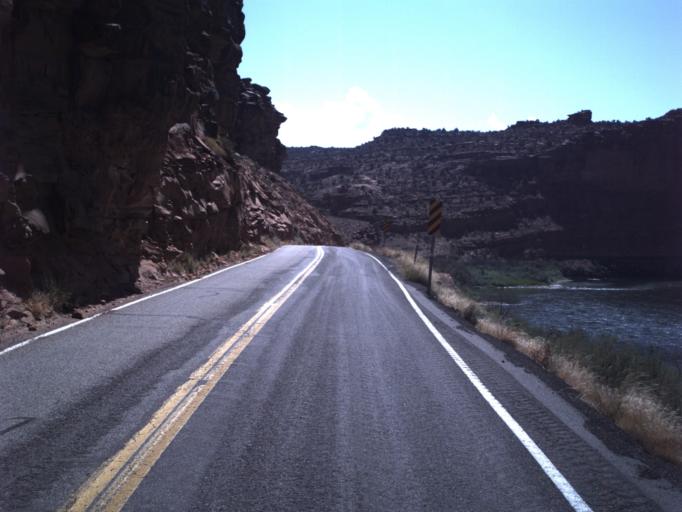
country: US
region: Utah
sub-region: Grand County
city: Moab
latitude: 38.8043
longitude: -109.3128
